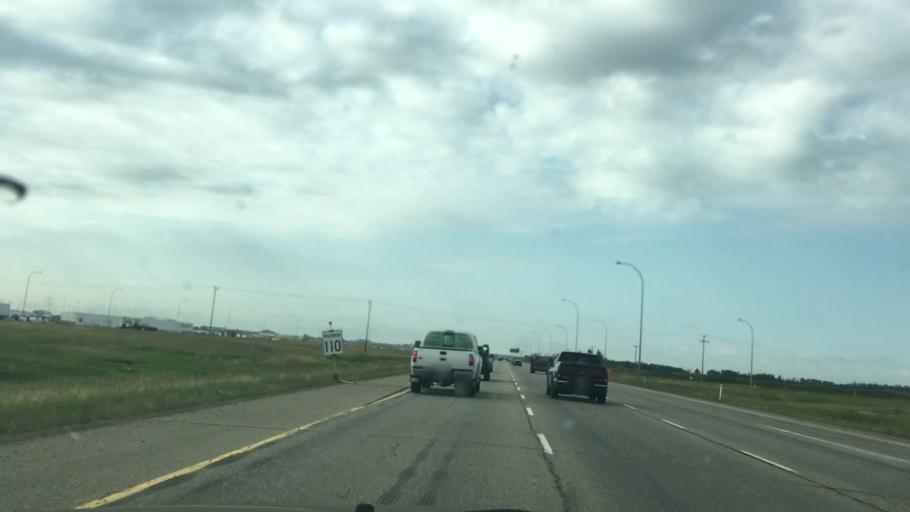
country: CA
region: Alberta
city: Leduc
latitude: 53.3367
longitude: -113.5503
